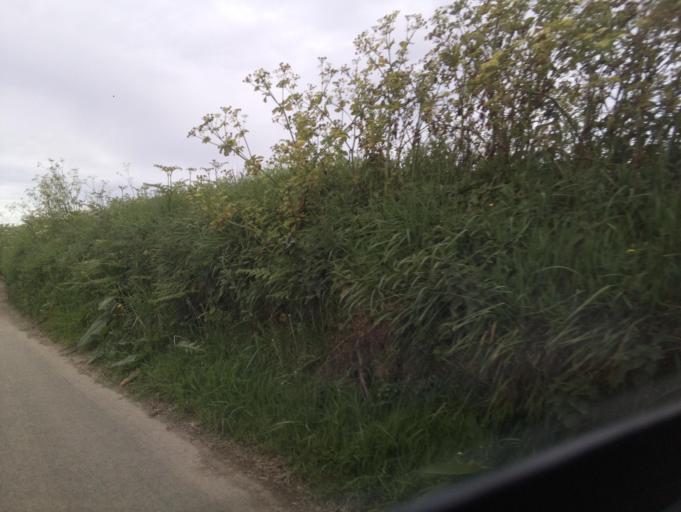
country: GB
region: England
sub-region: Devon
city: Dartmouth
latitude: 50.3443
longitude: -3.6552
